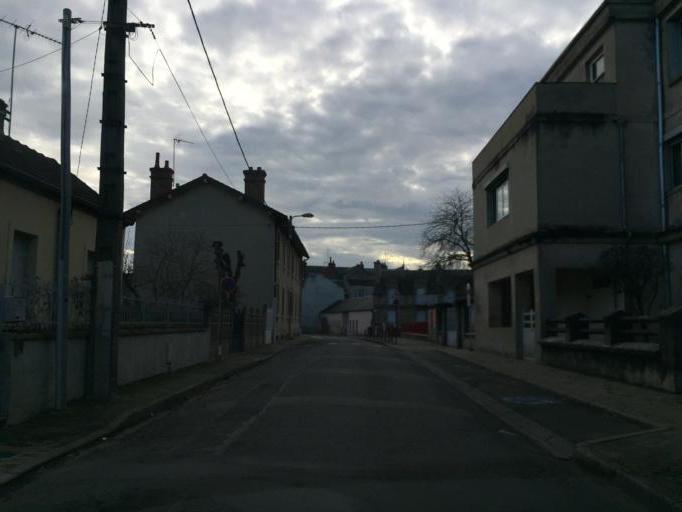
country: FR
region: Auvergne
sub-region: Departement de l'Allier
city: Moulins
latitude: 46.5706
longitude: 3.3372
